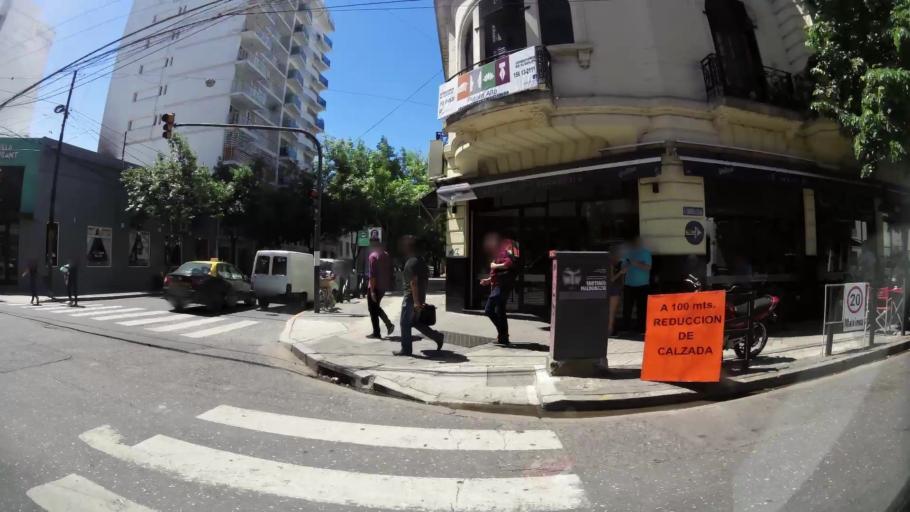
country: AR
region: Santa Fe
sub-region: Departamento de Rosario
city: Rosario
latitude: -32.9435
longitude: -60.6545
